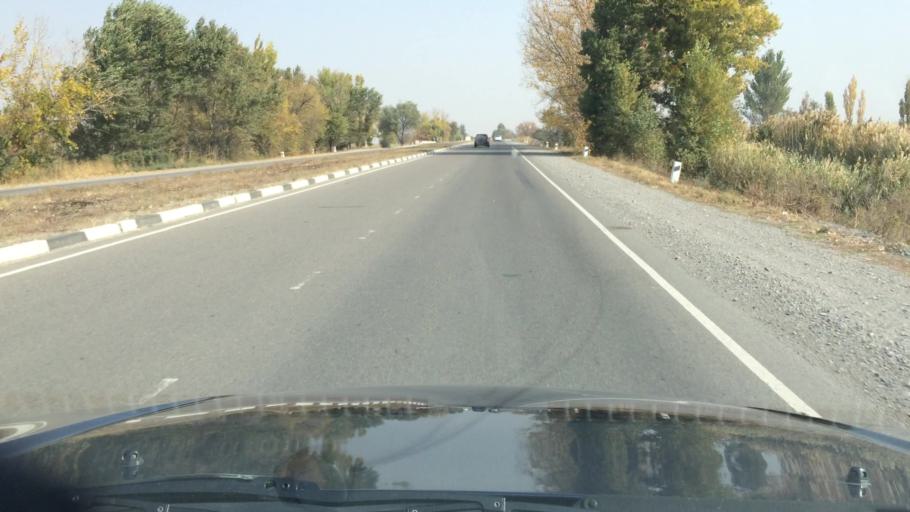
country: KG
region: Chuy
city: Kant
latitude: 42.9539
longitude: 74.7916
